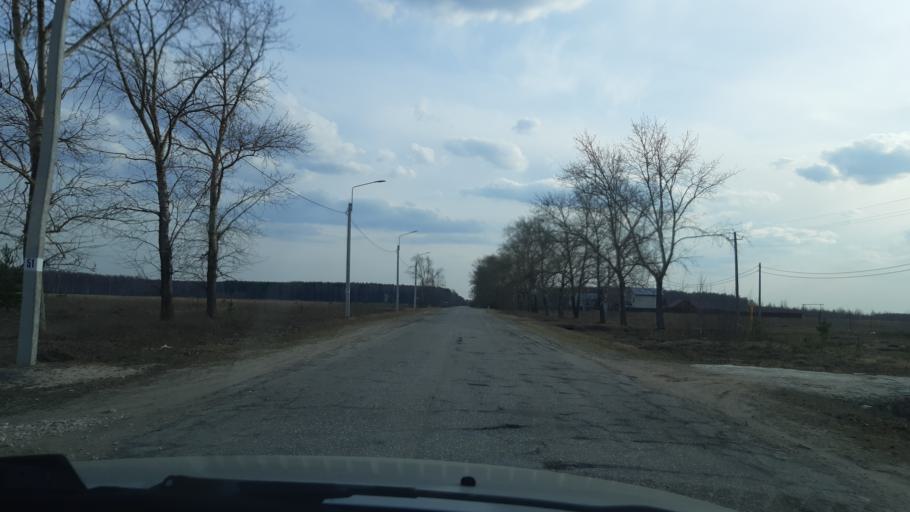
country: RU
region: Vladimir
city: Nikologory
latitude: 56.1272
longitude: 41.9889
